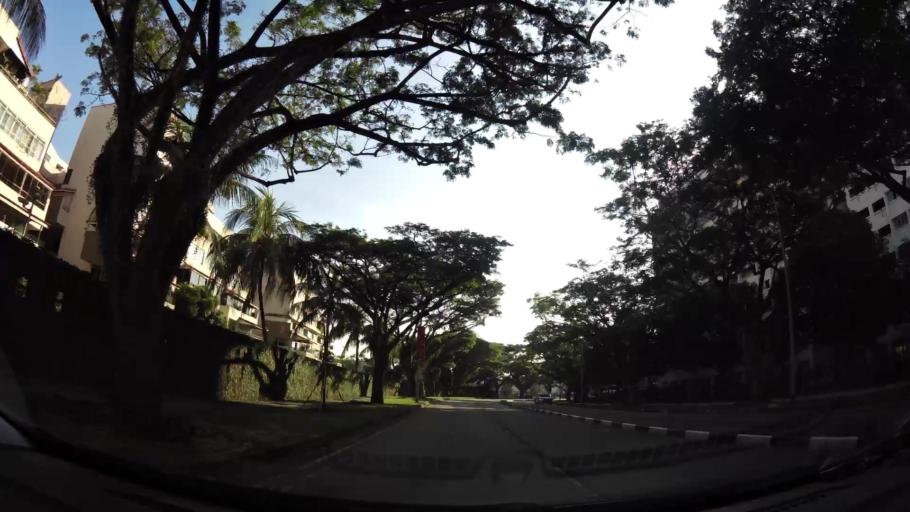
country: SG
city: Singapore
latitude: 1.3212
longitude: 103.9449
